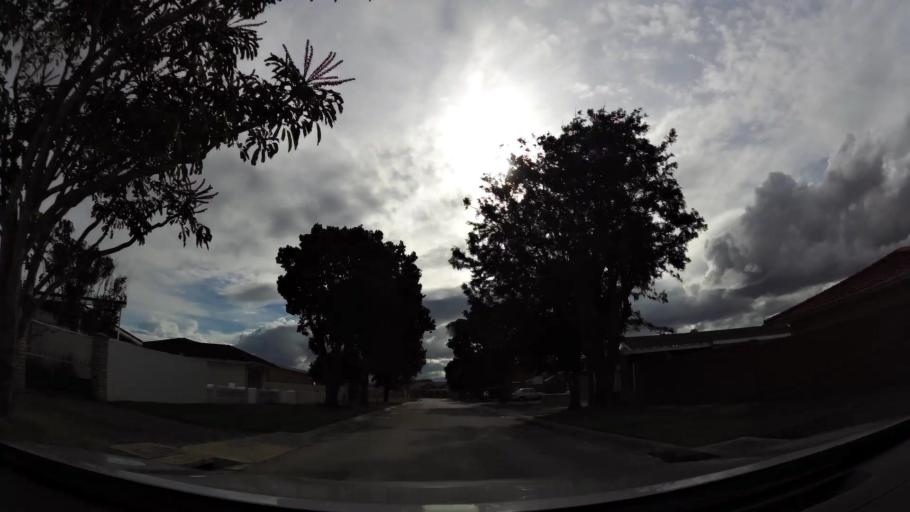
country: ZA
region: Eastern Cape
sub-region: Nelson Mandela Bay Metropolitan Municipality
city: Port Elizabeth
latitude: -33.9373
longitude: 25.5032
